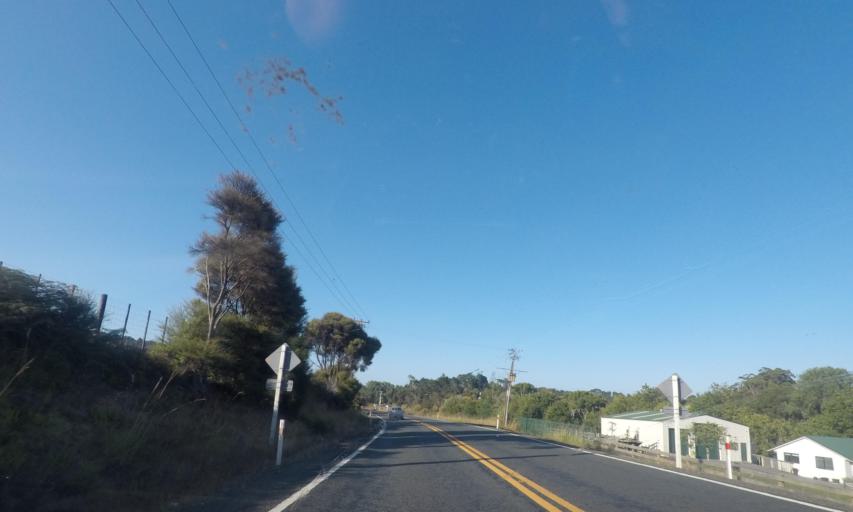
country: NZ
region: Auckland
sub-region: Auckland
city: Muriwai Beach
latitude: -36.7782
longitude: 174.4840
